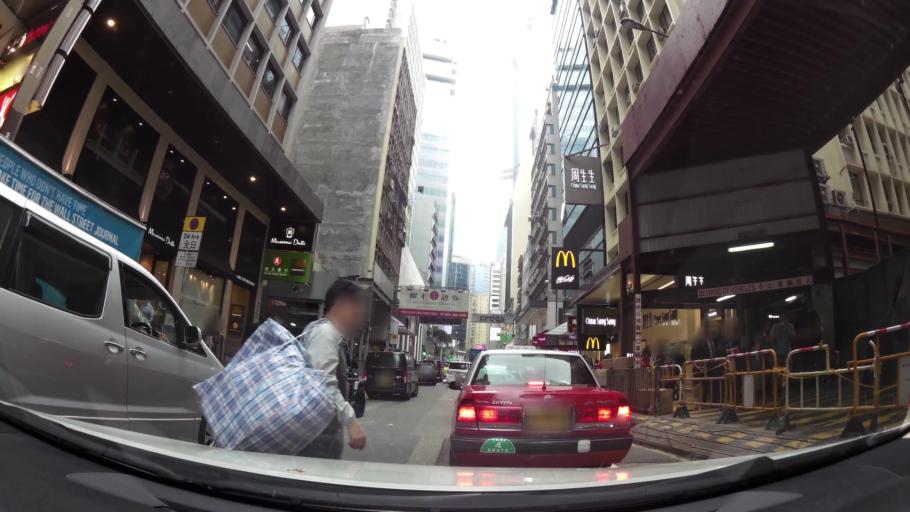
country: HK
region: Central and Western
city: Central
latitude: 22.2821
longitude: 114.1557
